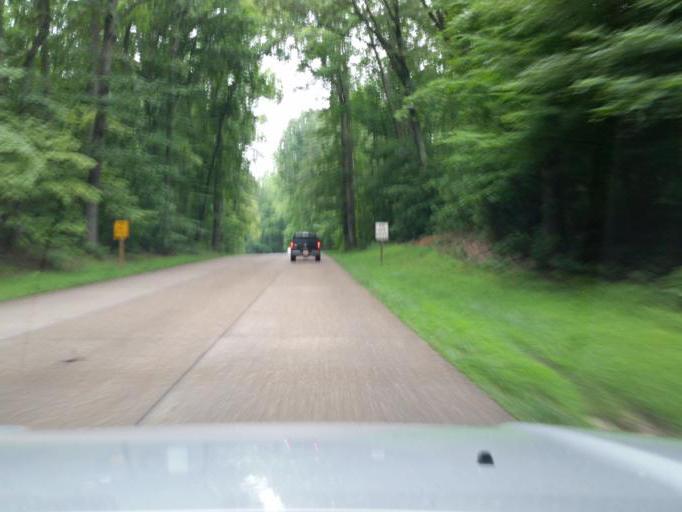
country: US
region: Virginia
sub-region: City of Williamsburg
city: Williamsburg
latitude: 37.2737
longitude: -76.6072
